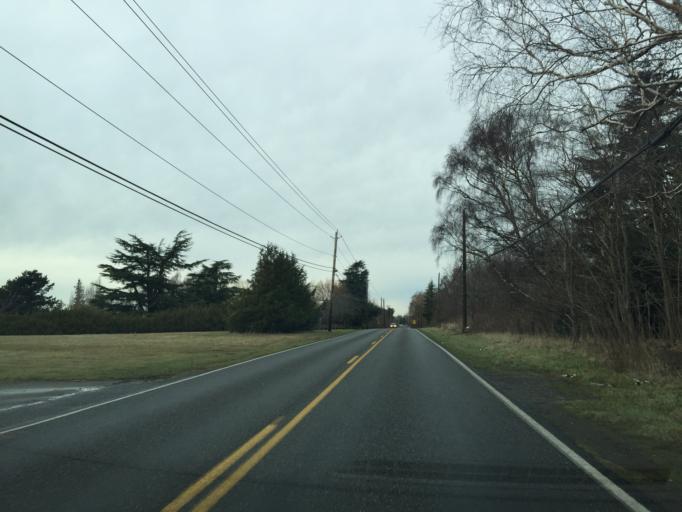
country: US
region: Washington
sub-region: Whatcom County
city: Marietta-Alderwood
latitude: 48.7772
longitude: -122.5358
